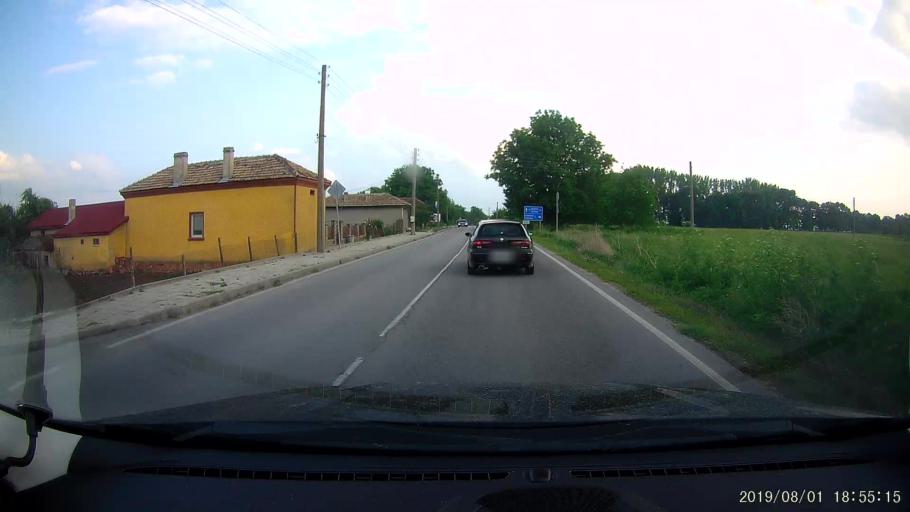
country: BG
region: Shumen
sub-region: Obshtina Smyadovo
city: Smyadovo
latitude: 43.1835
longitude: 27.0049
